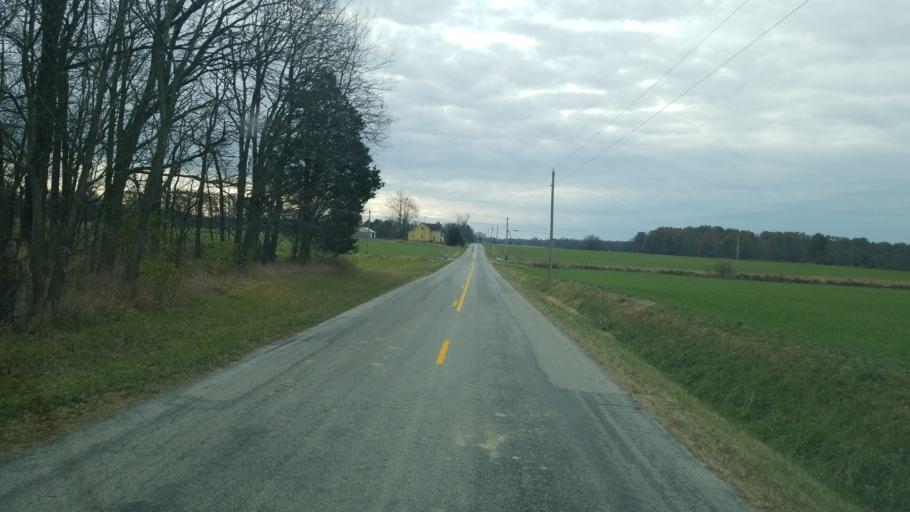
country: US
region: Ohio
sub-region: Morrow County
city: Cardington
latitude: 40.5516
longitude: -82.9767
